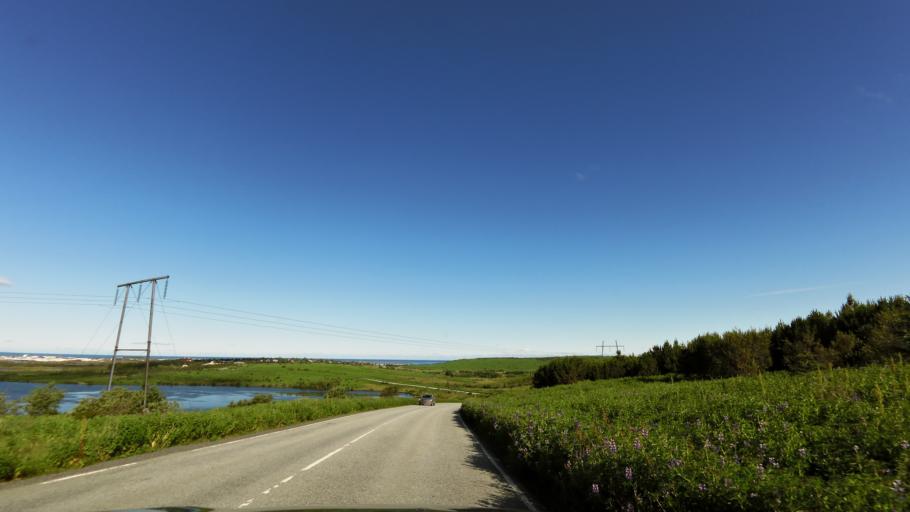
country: IS
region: Capital Region
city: Kopavogur
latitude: 64.0791
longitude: -21.8608
